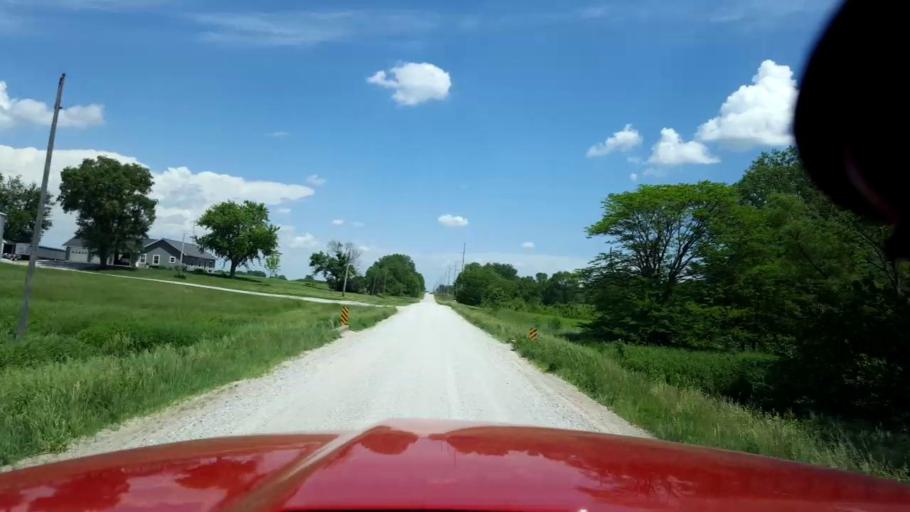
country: US
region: Iowa
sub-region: Boone County
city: Boone
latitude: 42.0493
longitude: -93.7608
